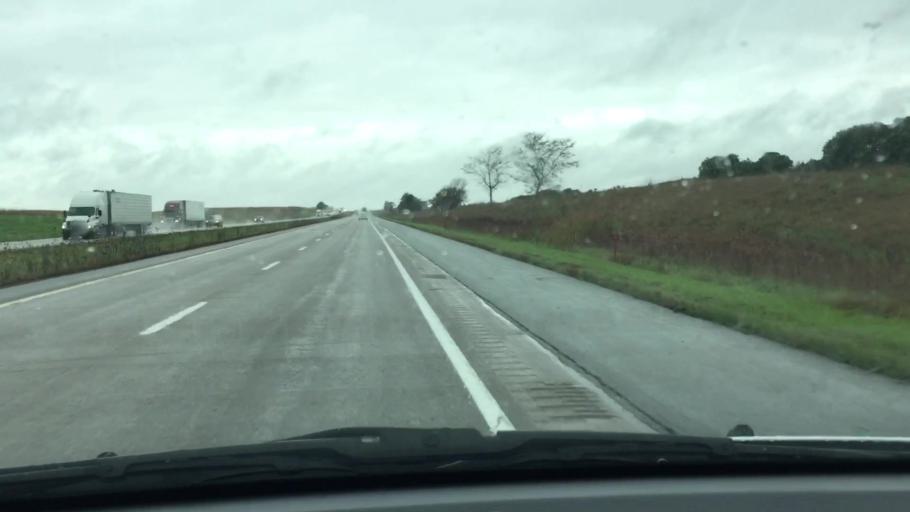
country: US
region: Iowa
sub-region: Poweshiek County
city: Brooklyn
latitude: 41.6950
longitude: -92.4842
